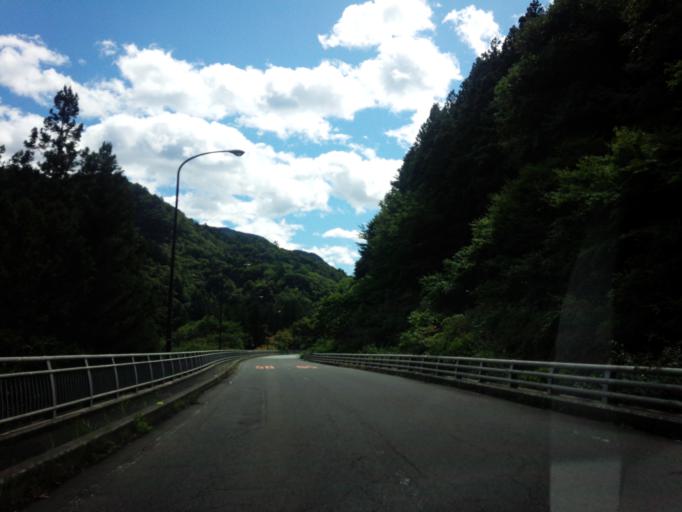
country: JP
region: Gunma
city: Nakanojomachi
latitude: 36.6808
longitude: 138.7793
